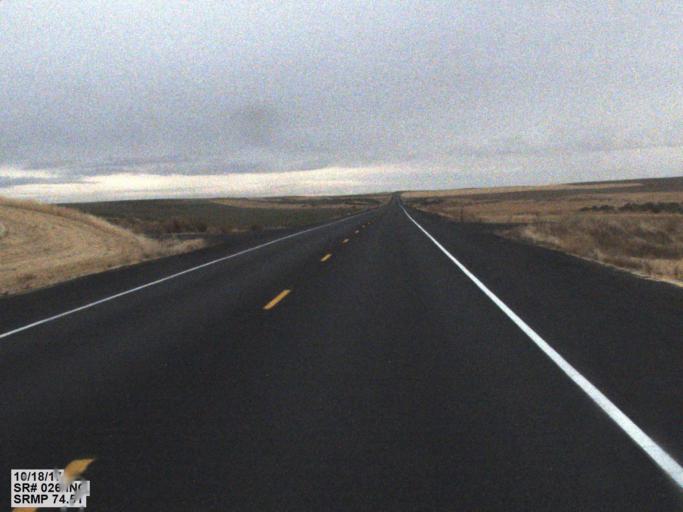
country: US
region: Washington
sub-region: Adams County
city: Ritzville
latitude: 46.7954
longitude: -118.4648
